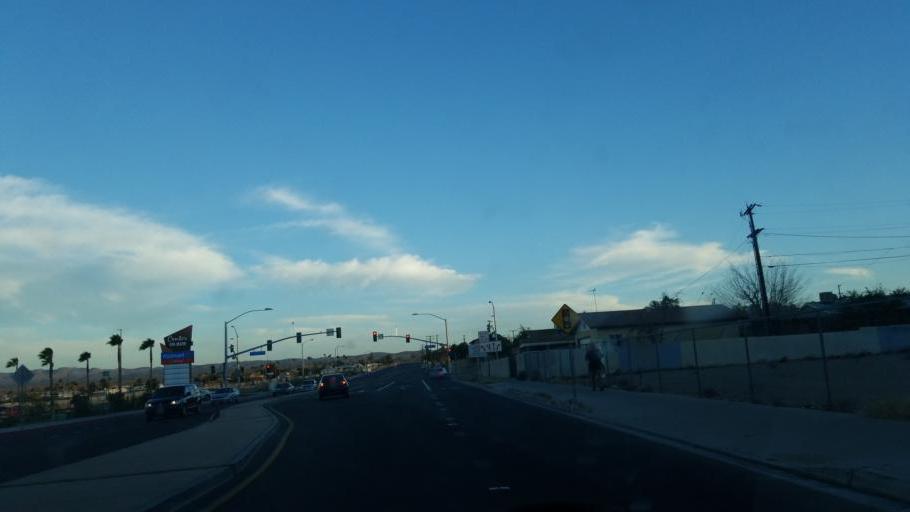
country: US
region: California
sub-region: San Bernardino County
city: Barstow
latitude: 34.8849
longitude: -116.9939
